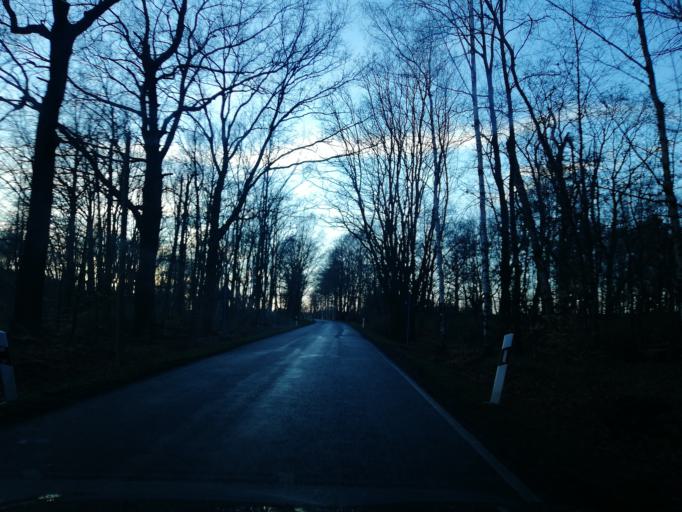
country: DE
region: Brandenburg
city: Calau
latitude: 51.7207
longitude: 13.9379
